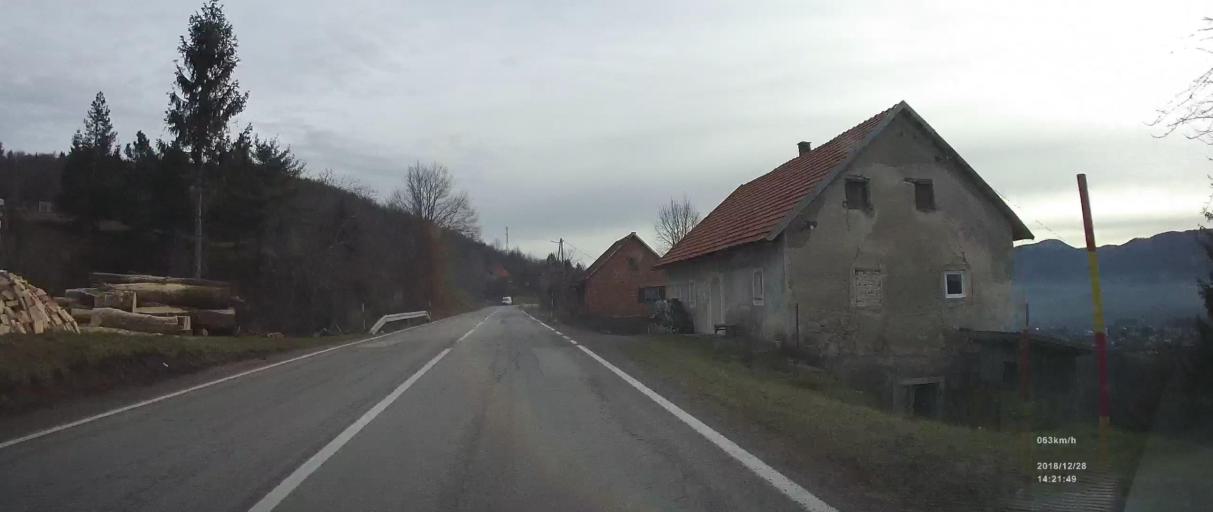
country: HR
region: Primorsko-Goranska
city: Vrbovsko
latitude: 45.3905
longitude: 15.0836
